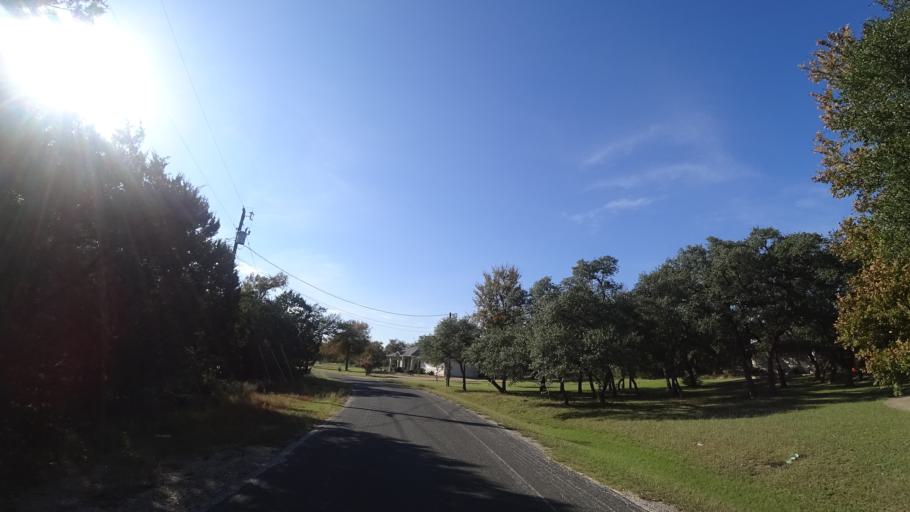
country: US
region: Texas
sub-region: Travis County
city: Bee Cave
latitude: 30.2378
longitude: -97.9287
